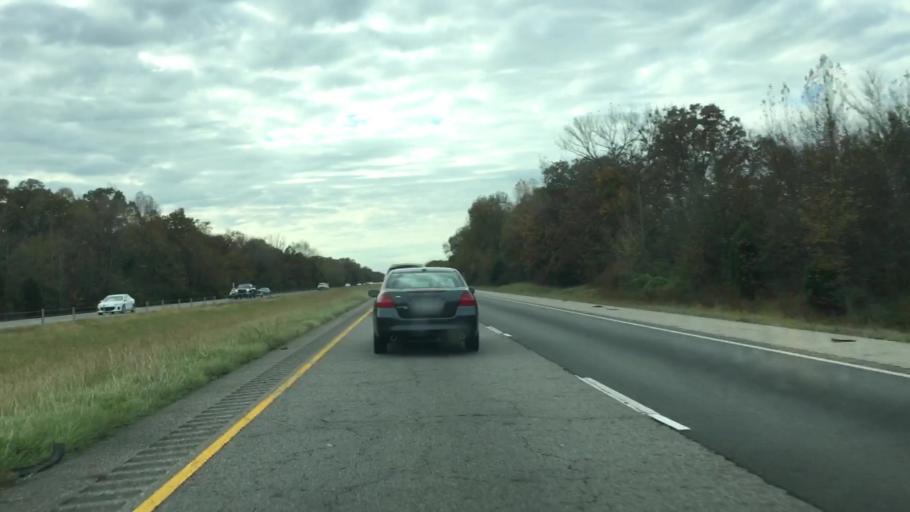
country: US
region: Arkansas
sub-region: Conway County
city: Morrilton
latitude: 35.1607
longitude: -92.5953
